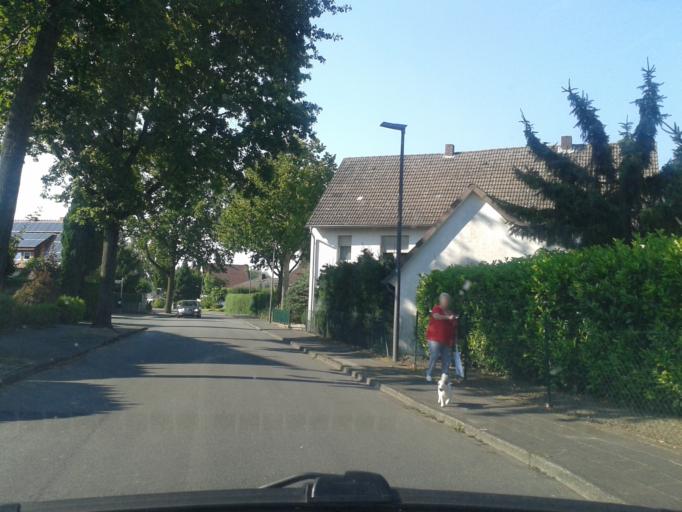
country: DE
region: North Rhine-Westphalia
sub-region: Regierungsbezirk Detmold
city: Paderborn
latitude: 51.7449
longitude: 8.6823
